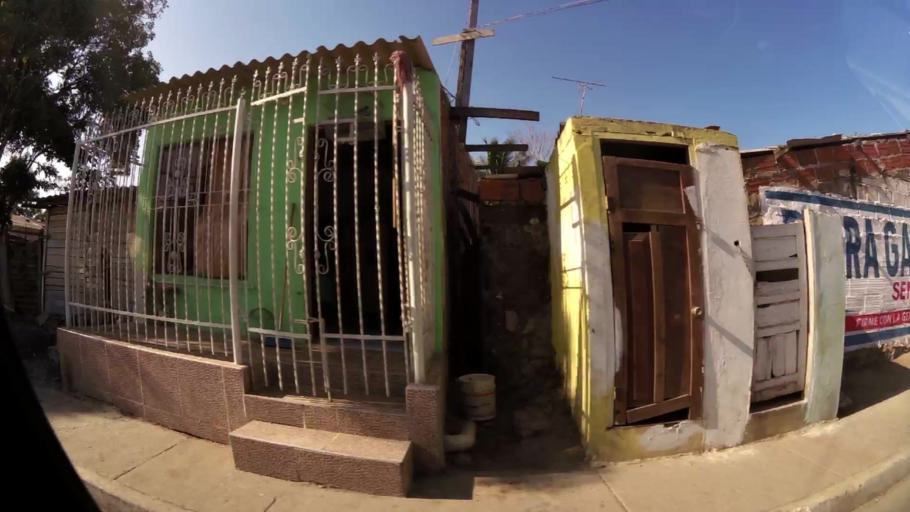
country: CO
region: Bolivar
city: Cartagena
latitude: 10.4788
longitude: -75.4914
